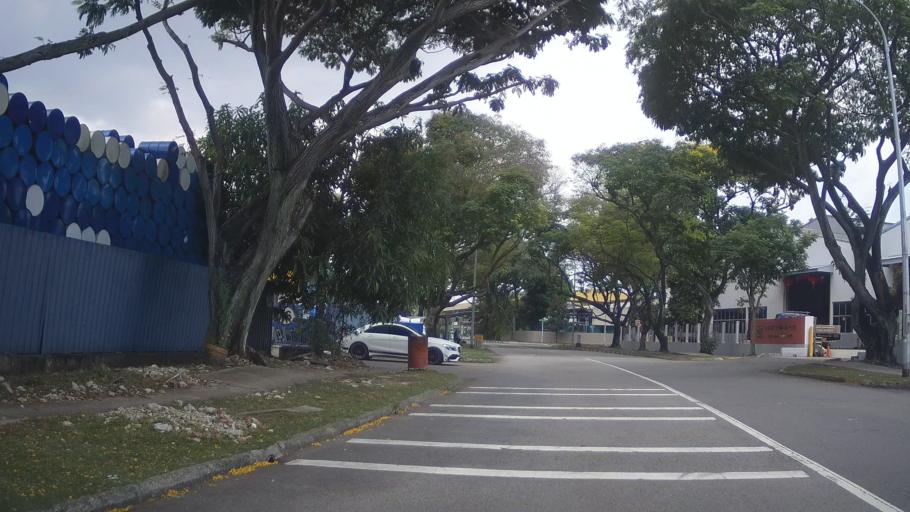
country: MY
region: Johor
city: Johor Bahru
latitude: 1.3095
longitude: 103.6641
